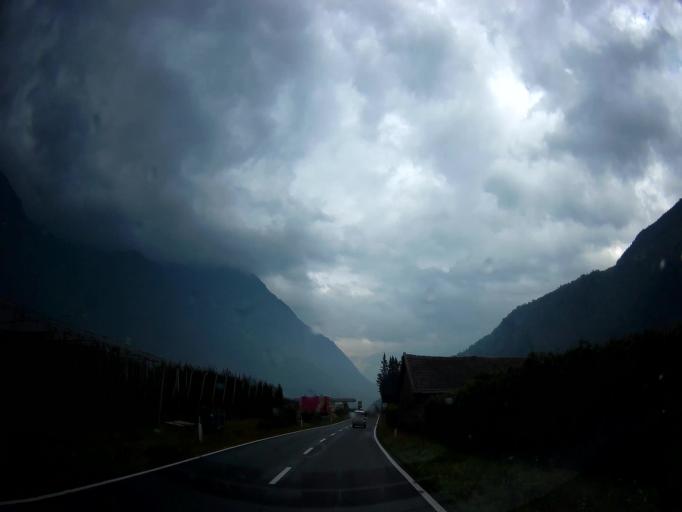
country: IT
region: Trentino-Alto Adige
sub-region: Bolzano
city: Rabla
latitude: 46.6725
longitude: 11.0732
